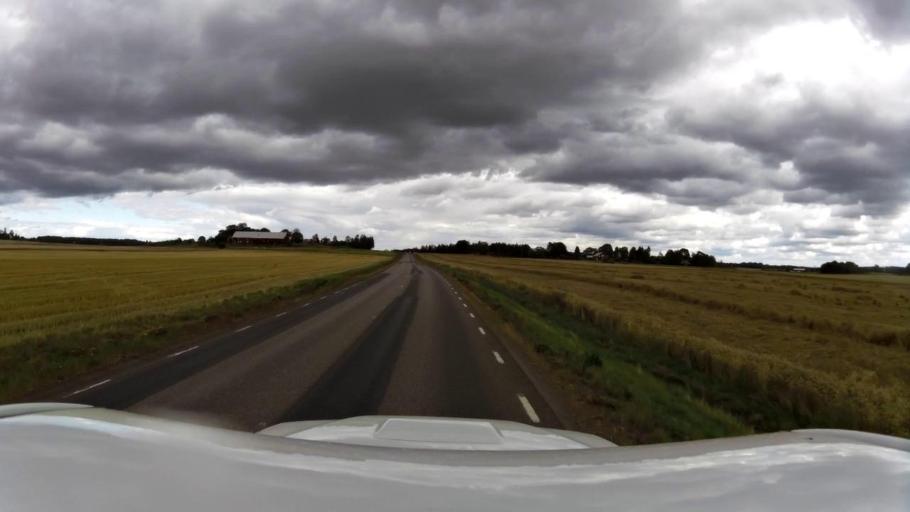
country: SE
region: OEstergoetland
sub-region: Linkopings Kommun
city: Linghem
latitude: 58.3918
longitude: 15.7553
